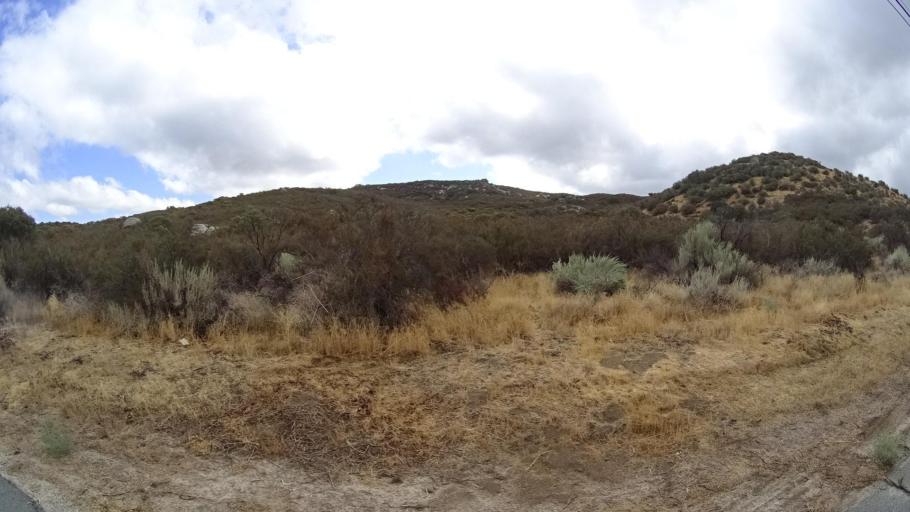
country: US
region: California
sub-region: San Diego County
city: Campo
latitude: 32.7065
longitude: -116.4315
